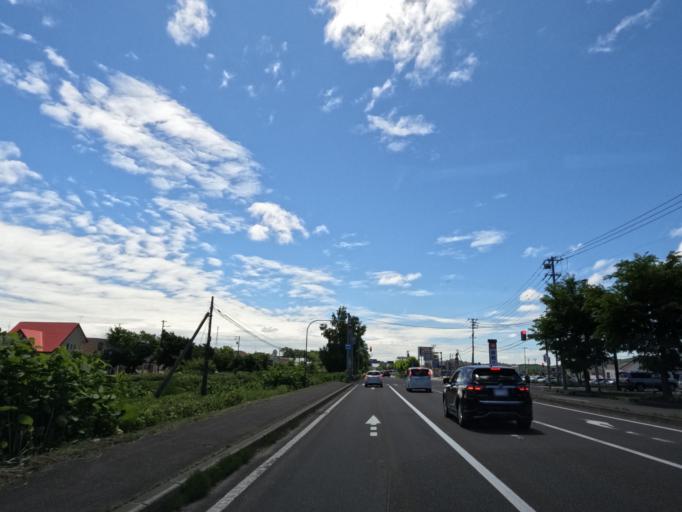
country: JP
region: Hokkaido
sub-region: Asahikawa-shi
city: Asahikawa
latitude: 43.7258
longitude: 142.3684
